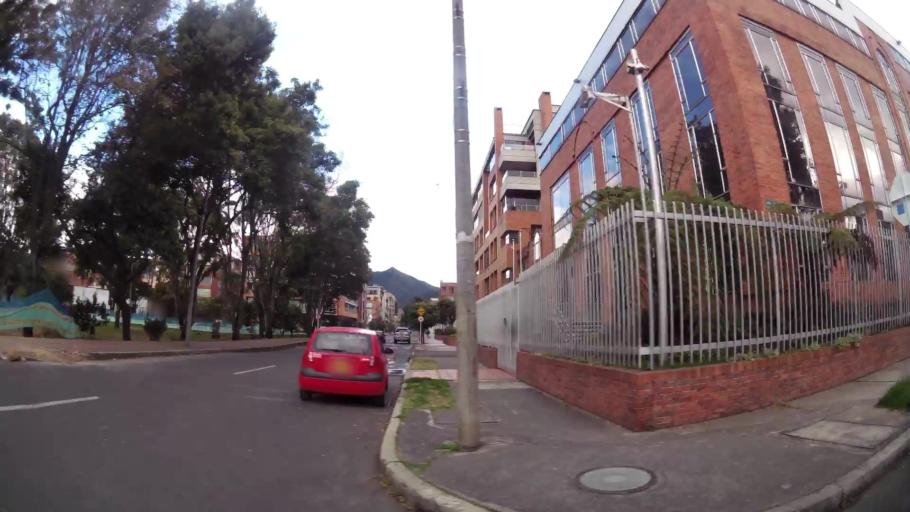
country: CO
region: Bogota D.C.
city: Barrio San Luis
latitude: 4.6876
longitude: -74.0509
